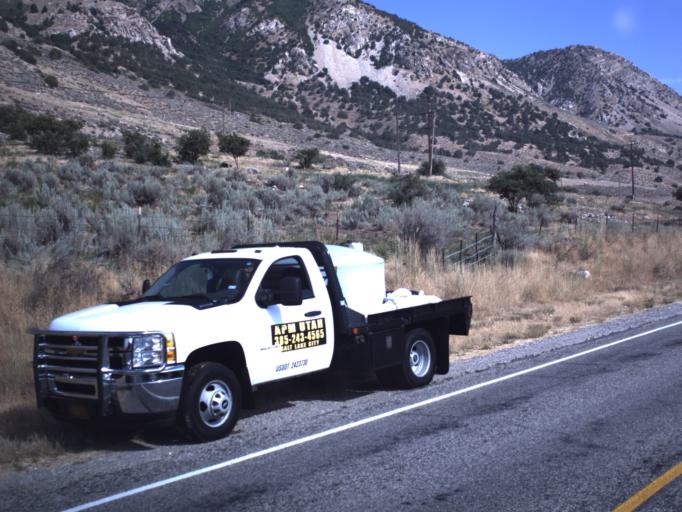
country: US
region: Utah
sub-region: Box Elder County
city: Brigham City
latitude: 41.5493
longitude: -112.0177
